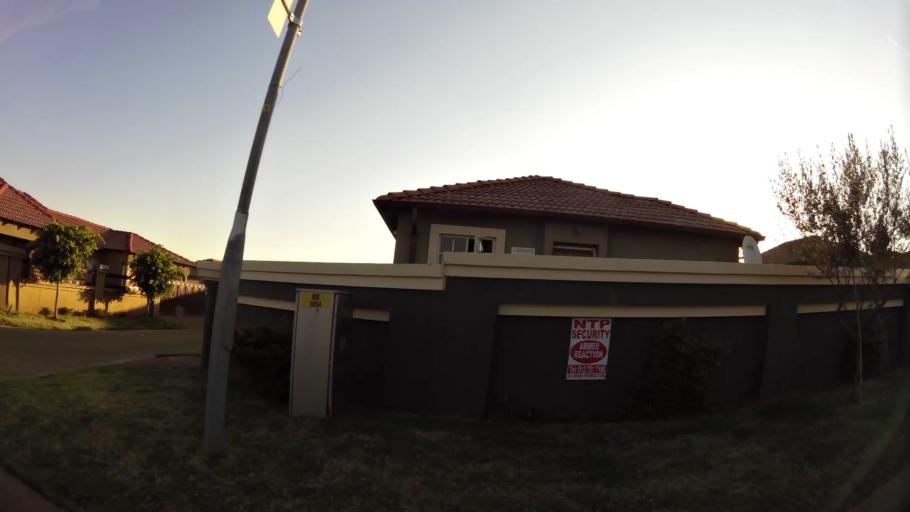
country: ZA
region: Gauteng
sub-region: City of Tshwane Metropolitan Municipality
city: Pretoria
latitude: -25.7435
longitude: 28.1055
